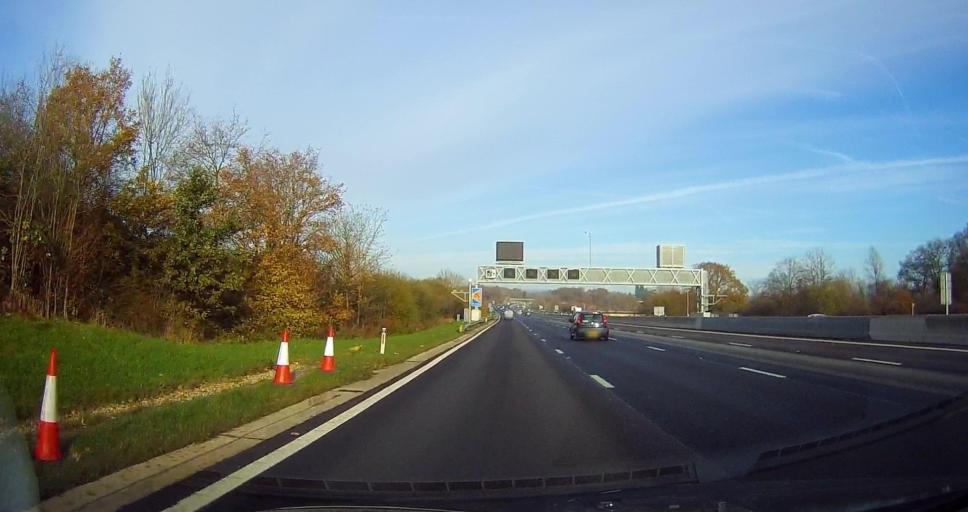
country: GB
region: England
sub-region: Surrey
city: Bletchingley
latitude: 51.2117
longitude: -0.1249
